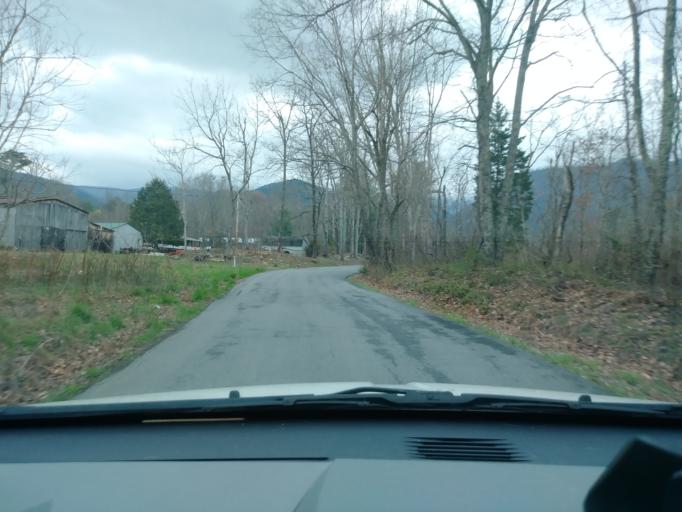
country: US
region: Tennessee
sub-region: Greene County
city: Tusculum
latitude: 36.0817
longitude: -82.7266
